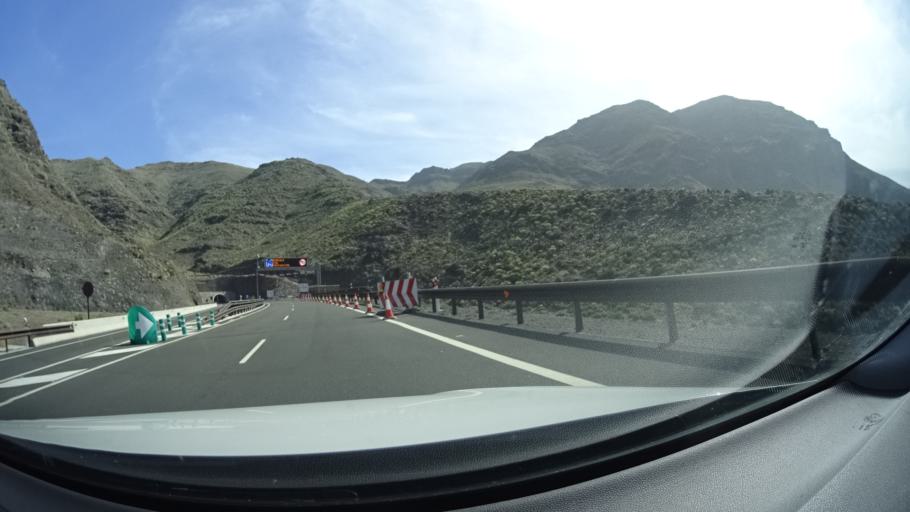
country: ES
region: Canary Islands
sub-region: Provincia de Las Palmas
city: San Nicolas
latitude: 28.0206
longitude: -15.7657
